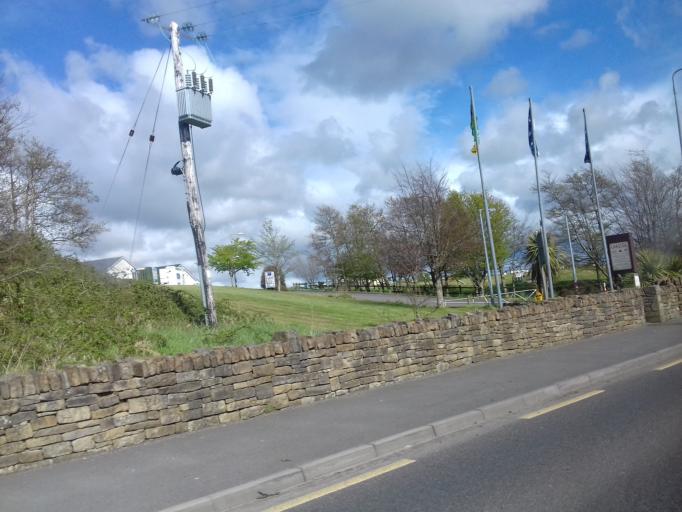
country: IE
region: Ulster
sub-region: County Donegal
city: Ballyshannon
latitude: 54.4968
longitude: -8.1739
